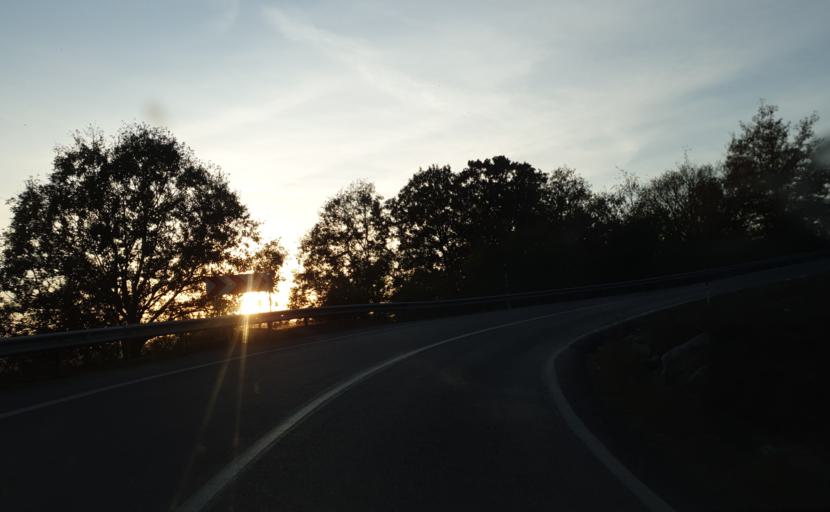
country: TR
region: Kirklareli
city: Sergen
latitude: 41.8373
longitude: 27.7947
